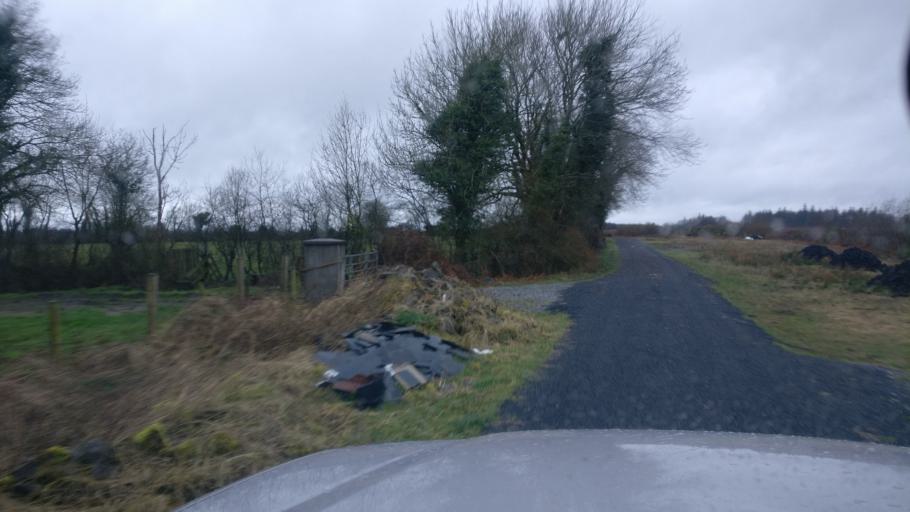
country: IE
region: Connaught
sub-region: County Galway
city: Ballinasloe
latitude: 53.2463
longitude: -8.3298
